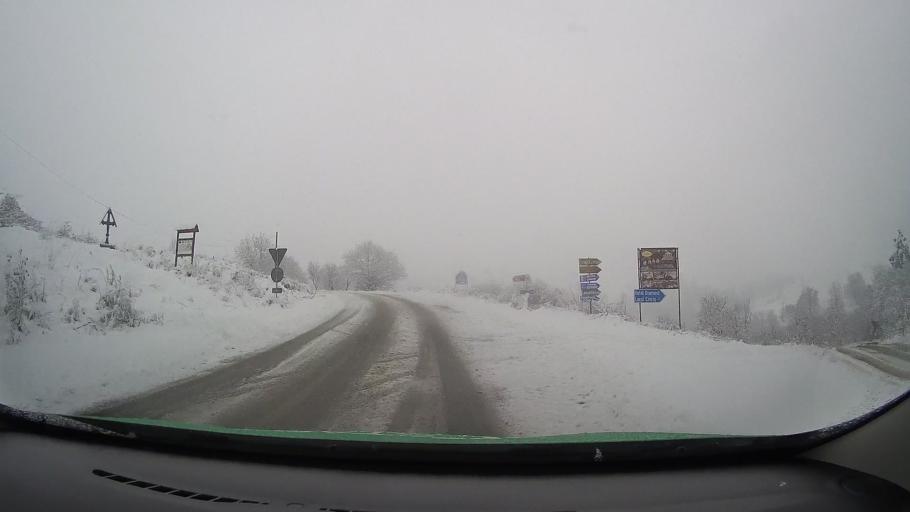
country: RO
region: Hunedoara
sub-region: Comuna Teliucu Inferior
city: Teliucu Inferior
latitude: 45.7039
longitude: 22.8815
